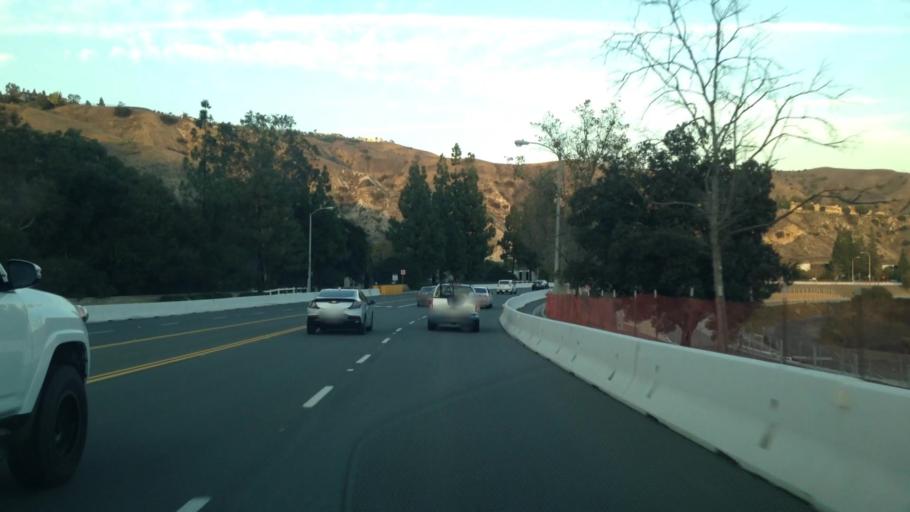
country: US
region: California
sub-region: Orange County
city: Yorba Linda
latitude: 33.8813
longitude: -117.7428
